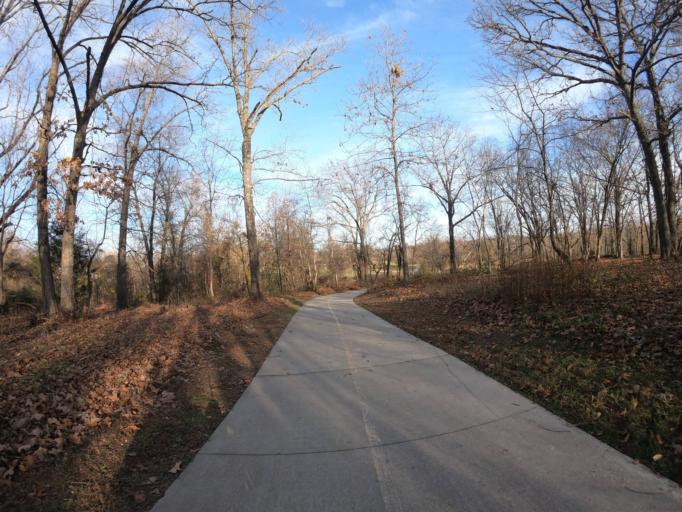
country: US
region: Arkansas
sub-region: Benton County
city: Rogers
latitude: 36.3330
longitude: -94.1670
